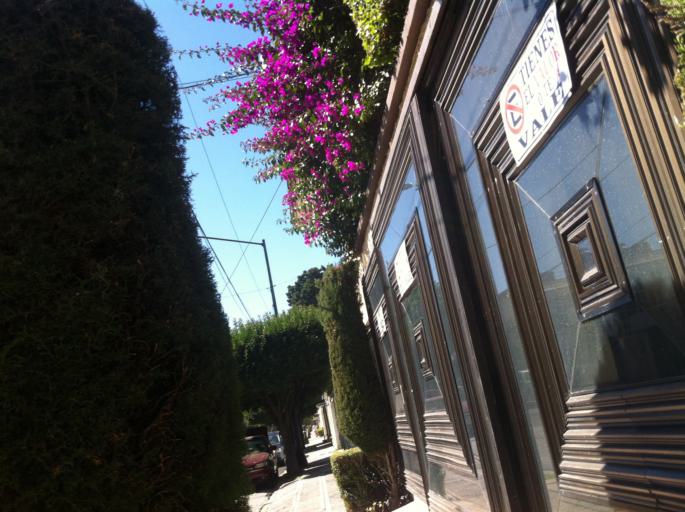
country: MX
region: Mexico
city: Colonia Lindavista
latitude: 19.4955
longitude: -99.1259
